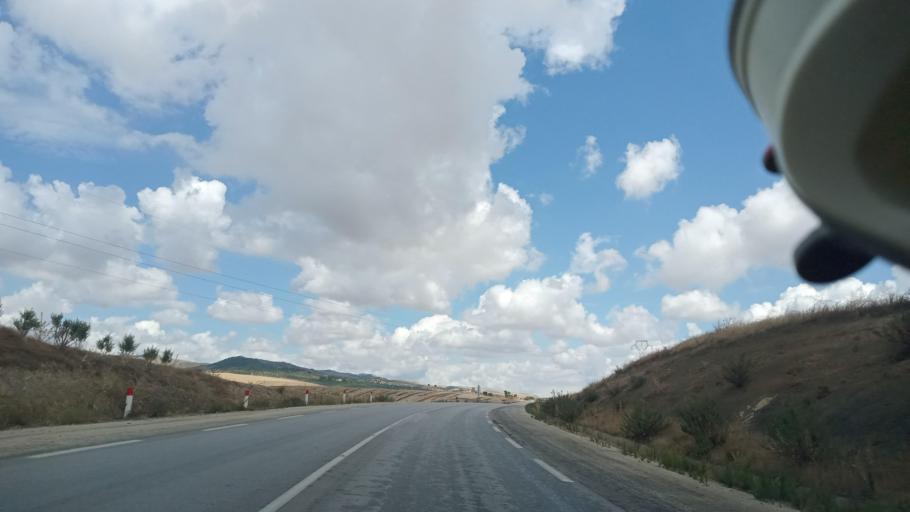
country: TN
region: Silyanah
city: Al Karib
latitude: 36.3012
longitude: 9.0817
